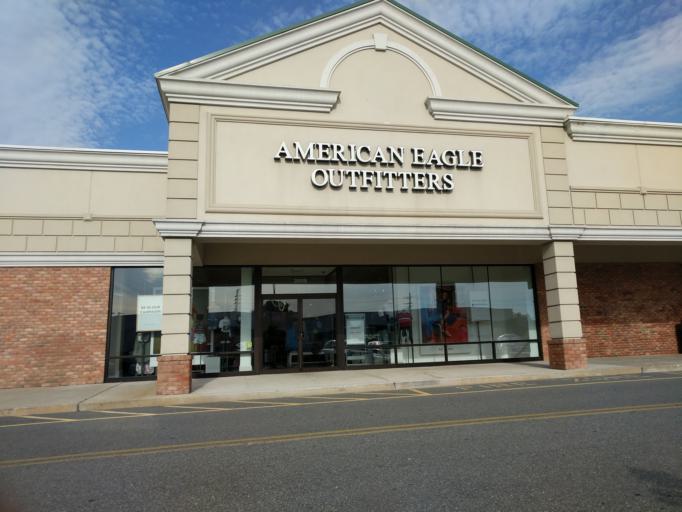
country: US
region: New York
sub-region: Nassau County
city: Oceanside
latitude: 40.6253
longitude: -73.6383
